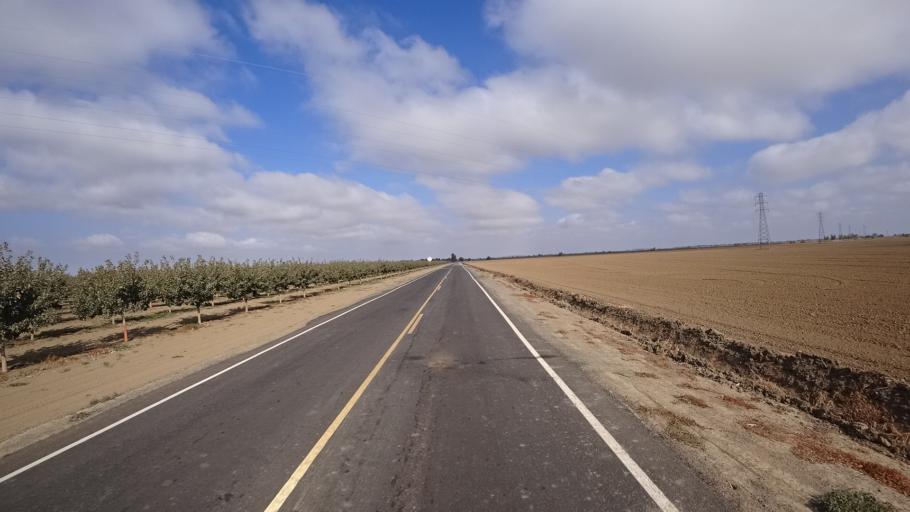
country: US
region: California
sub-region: Yolo County
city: Woodland
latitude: 38.7939
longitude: -121.7746
